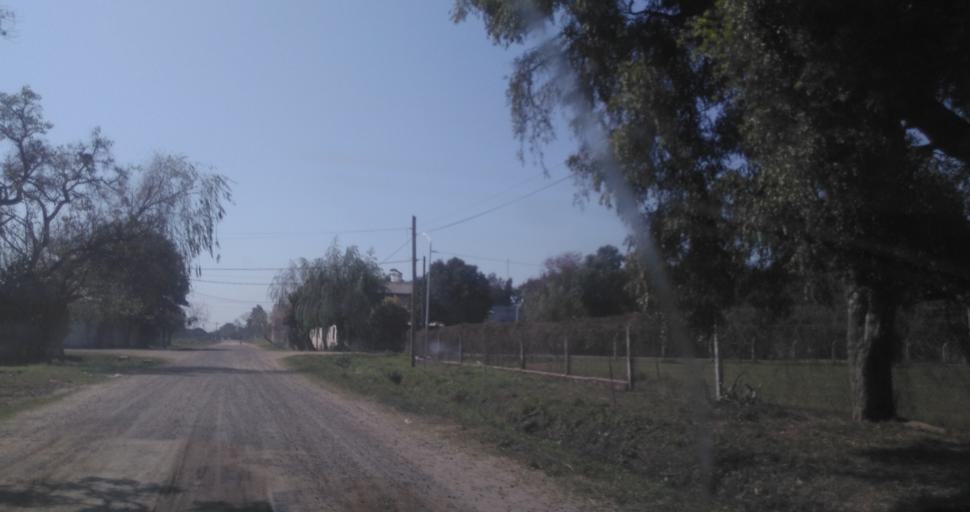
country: AR
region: Chaco
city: Fontana
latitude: -27.4307
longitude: -59.0302
